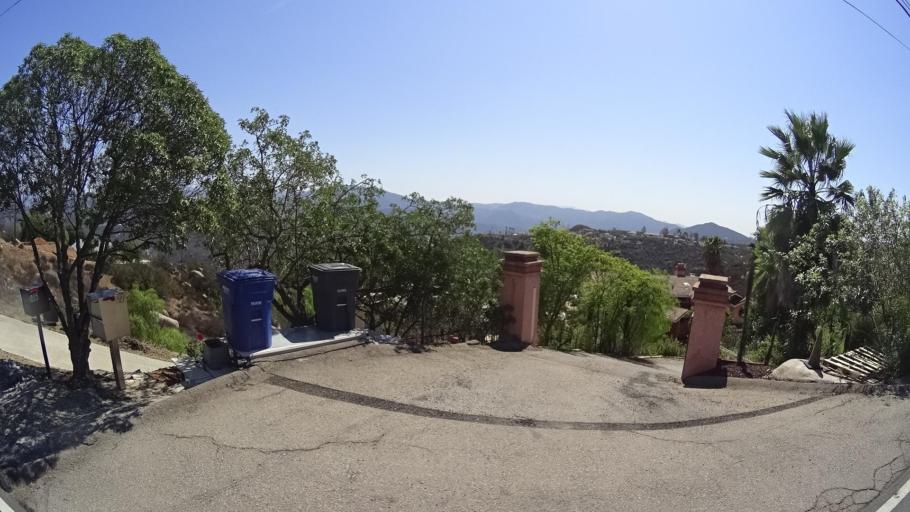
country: US
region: California
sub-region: San Diego County
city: Crest
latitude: 32.8208
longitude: -116.8516
